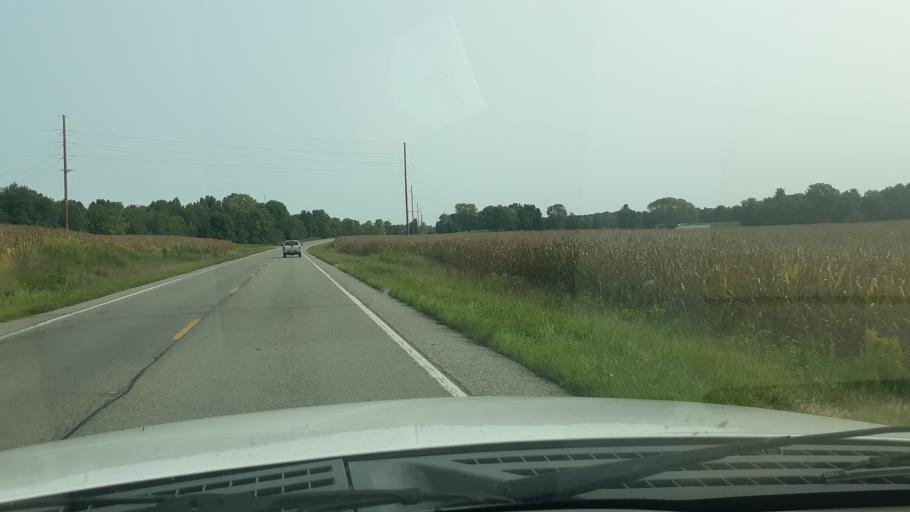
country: US
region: Illinois
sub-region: White County
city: Norris City
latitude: 37.9753
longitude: -88.3192
